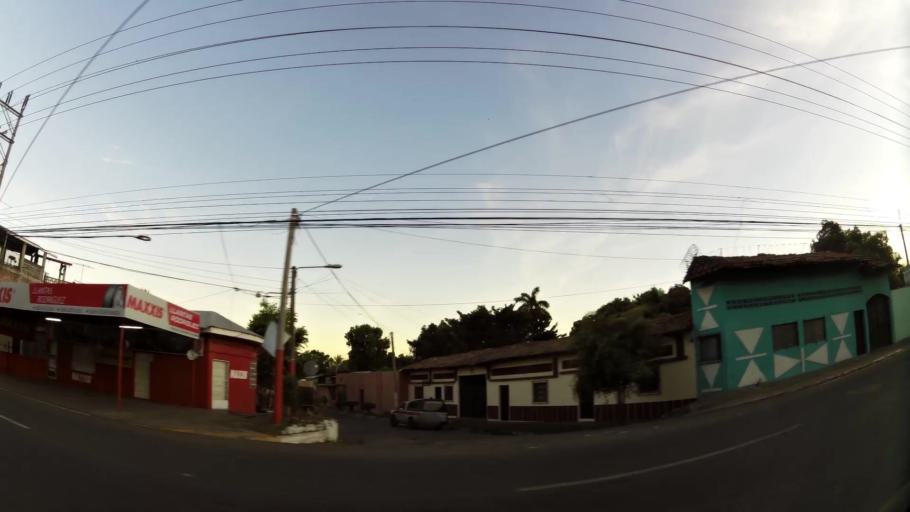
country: SV
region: San Miguel
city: San Miguel
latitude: 13.4901
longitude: -88.1812
